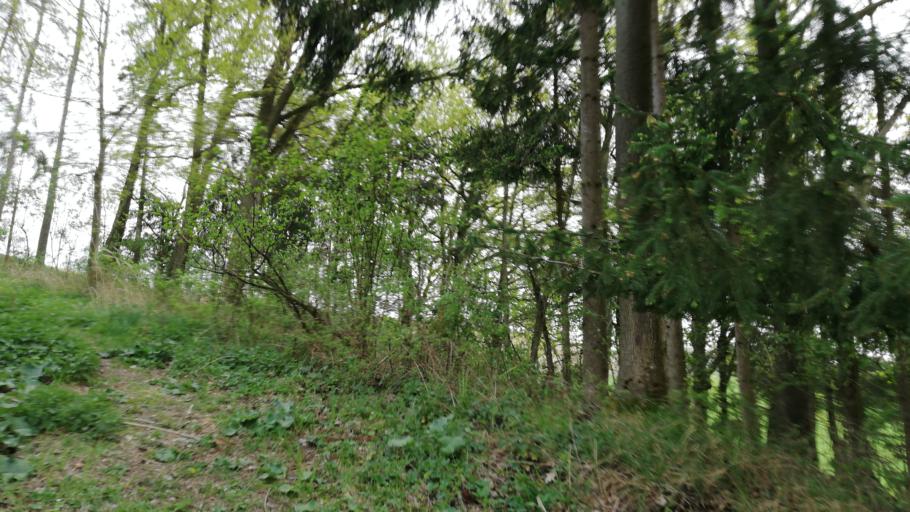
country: AT
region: Upper Austria
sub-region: Politischer Bezirk Grieskirchen
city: Bad Schallerbach
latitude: 48.1860
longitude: 13.9311
